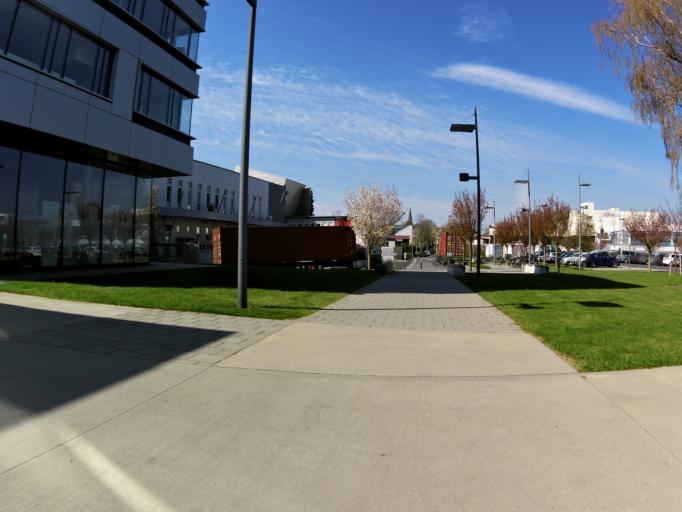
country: DE
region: Bavaria
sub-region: Regierungsbezirk Unterfranken
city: Rottendorf
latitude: 49.7925
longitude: 10.0333
